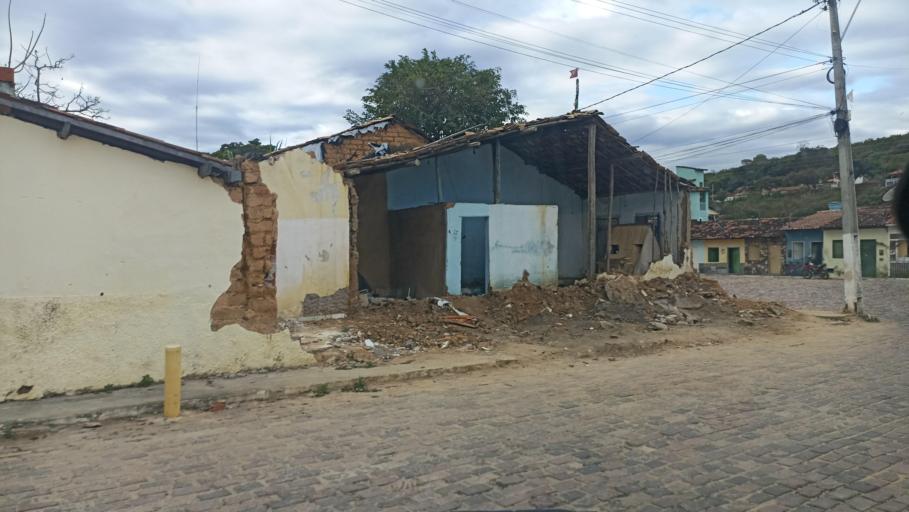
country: BR
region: Bahia
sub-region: Andarai
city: Vera Cruz
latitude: -12.8109
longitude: -41.3321
